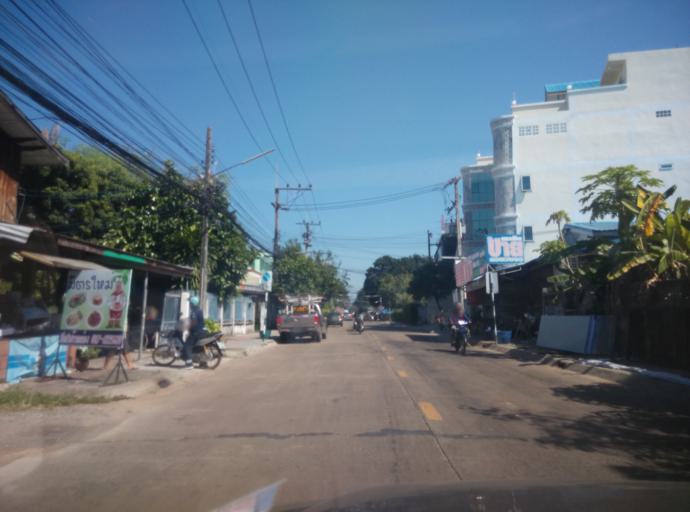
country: TH
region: Sisaket
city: Si Sa Ket
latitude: 15.1153
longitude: 104.3228
